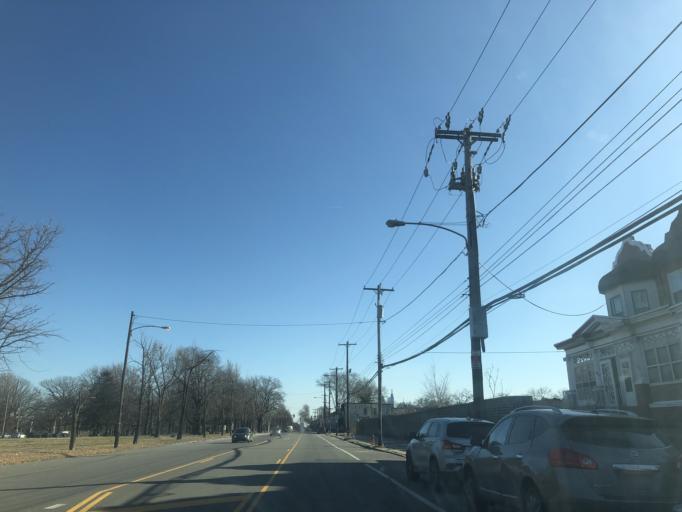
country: US
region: Pennsylvania
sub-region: Montgomery County
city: Bala-Cynwyd
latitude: 39.9789
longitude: -75.2164
